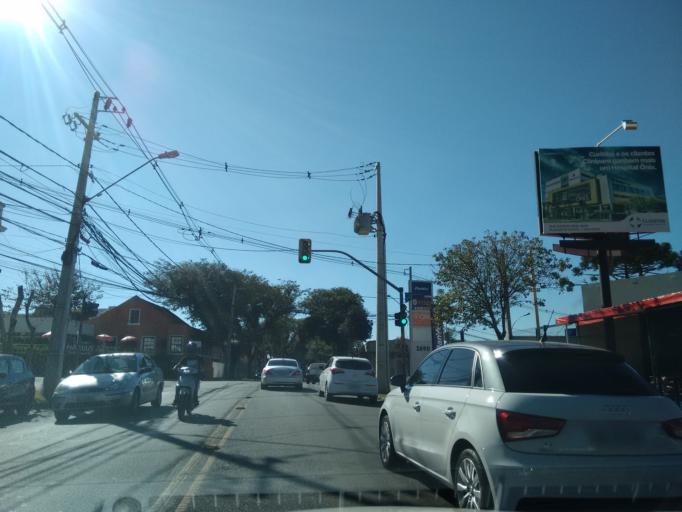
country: BR
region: Parana
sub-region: Curitiba
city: Curitiba
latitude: -25.4038
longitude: -49.2713
